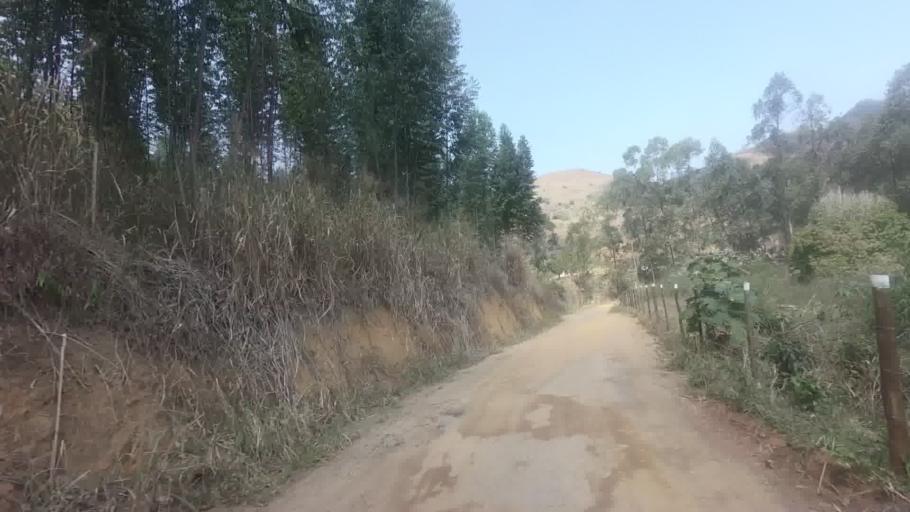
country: BR
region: Espirito Santo
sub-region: Sao Jose Do Calcado
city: Sao Jose do Calcado
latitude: -21.0442
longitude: -41.5243
